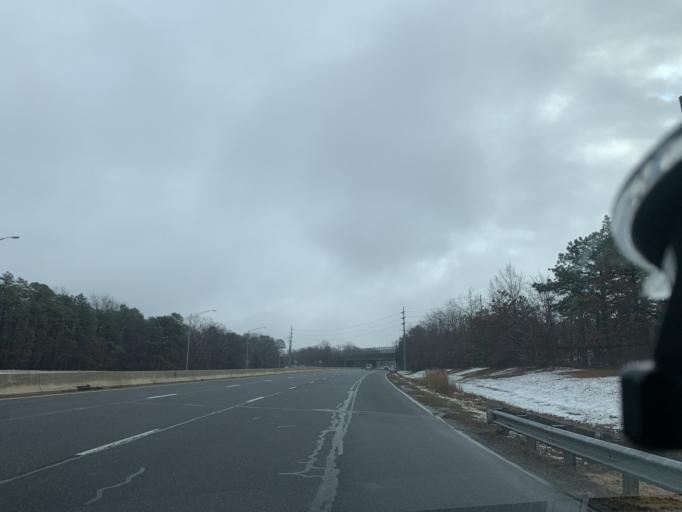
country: US
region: New Jersey
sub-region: Atlantic County
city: Pomona
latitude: 39.4354
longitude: -74.5894
